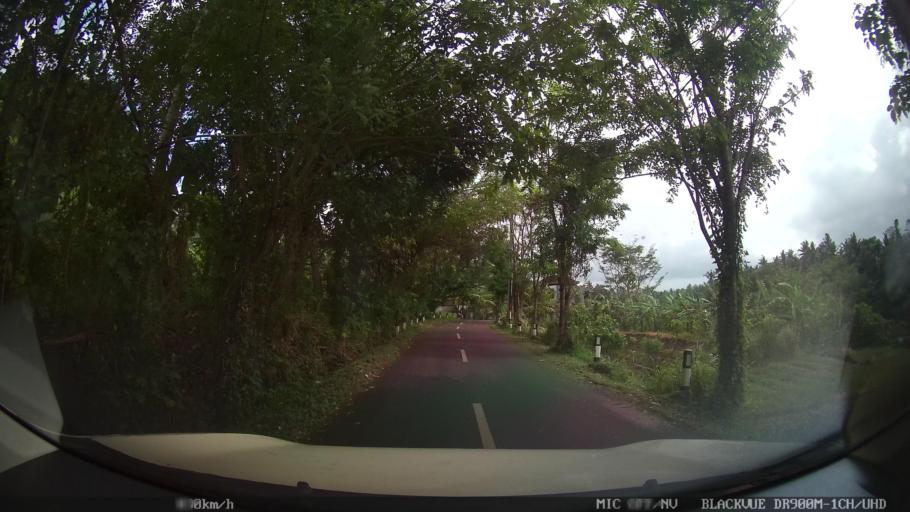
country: ID
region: Bali
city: Banjar Parekan
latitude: -8.5718
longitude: 115.2037
